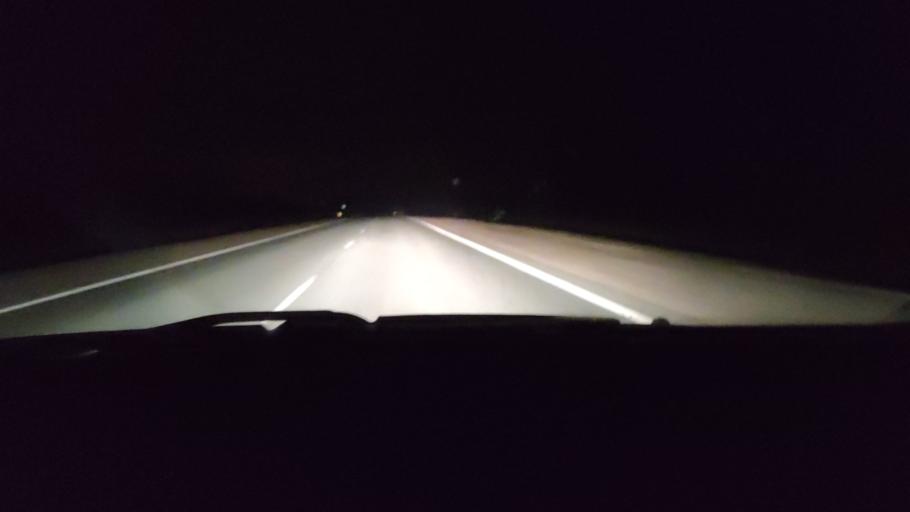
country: RU
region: Saratov
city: Dukhovnitskoye
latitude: 52.8519
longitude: 48.2578
